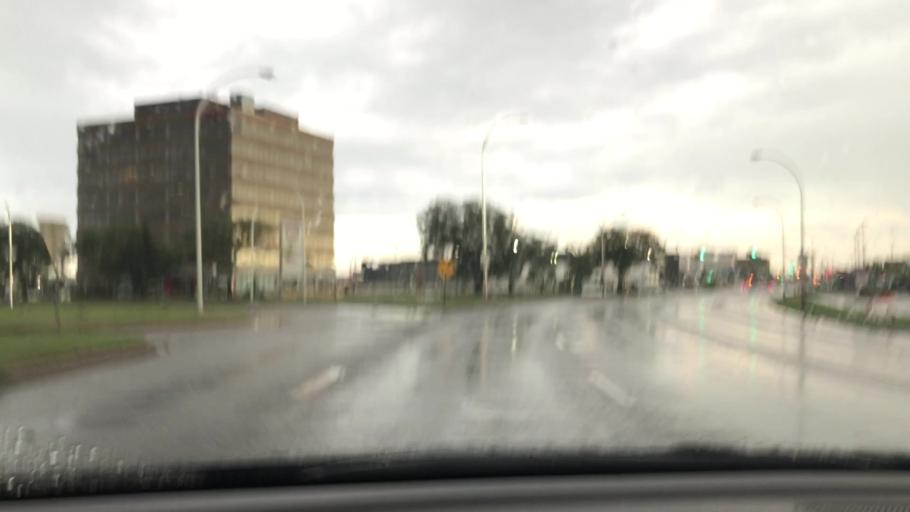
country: CA
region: Alberta
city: Edmonton
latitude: 53.4914
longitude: -113.4951
